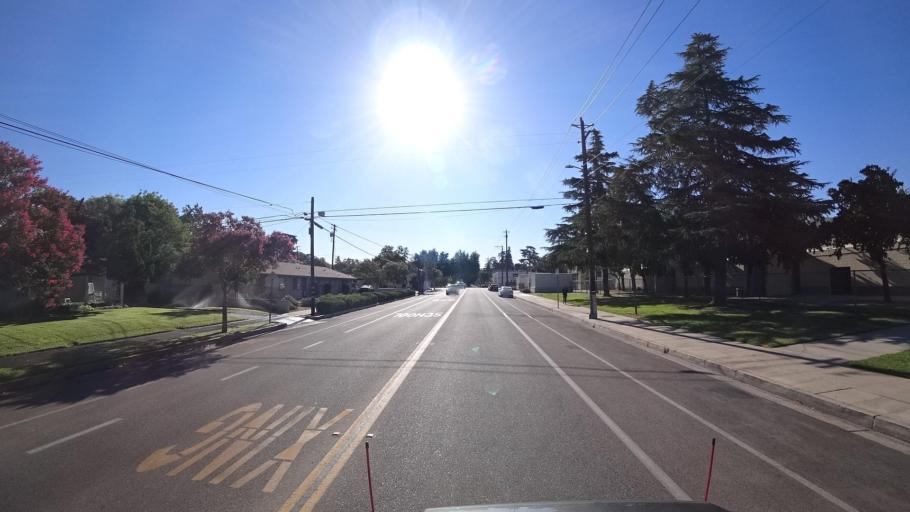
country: US
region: California
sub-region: Fresno County
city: Fresno
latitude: 36.7685
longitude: -119.8055
